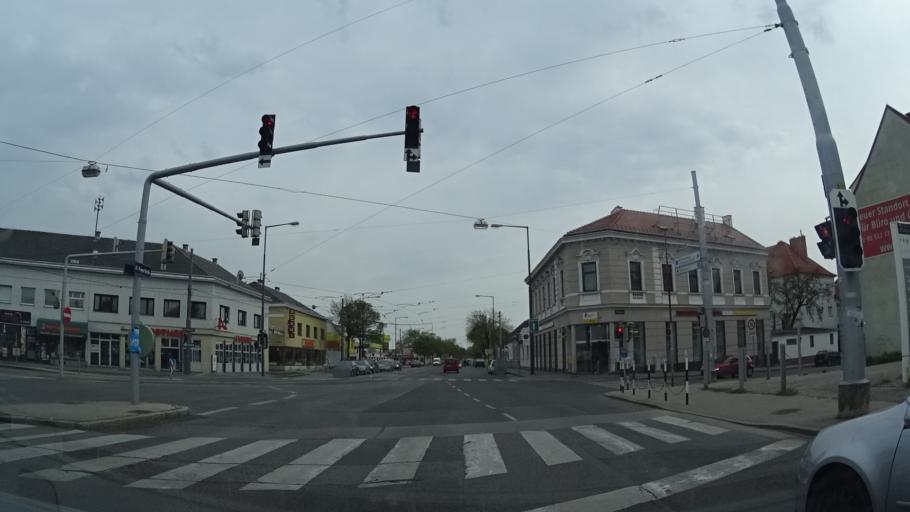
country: AT
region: Lower Austria
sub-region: Politischer Bezirk Korneuburg
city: Langenzersdorf
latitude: 48.2876
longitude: 16.3830
